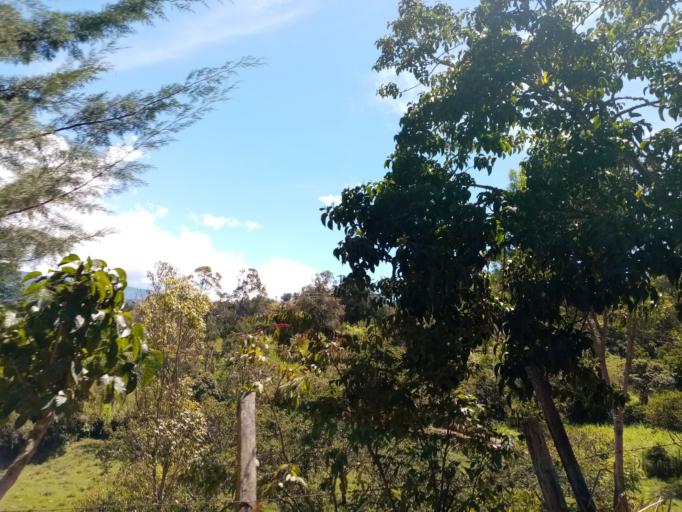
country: CO
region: Cundinamarca
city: Tenza
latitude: 5.0761
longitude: -73.4280
